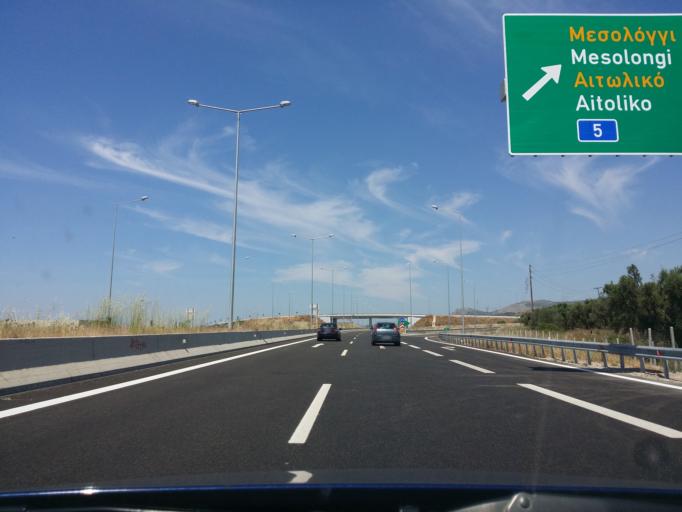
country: GR
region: West Greece
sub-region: Nomos Aitolias kai Akarnanias
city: Galatas
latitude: 38.3788
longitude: 21.5025
